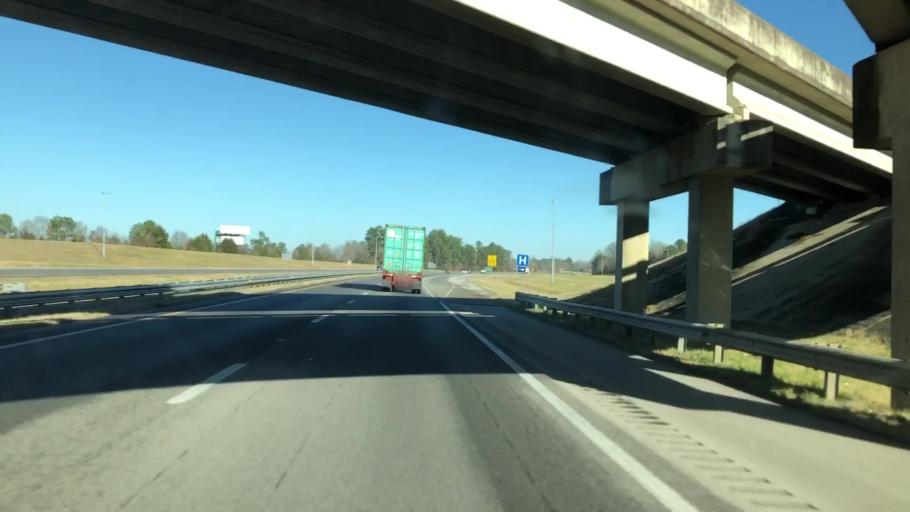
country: US
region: Alabama
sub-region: Limestone County
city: Athens
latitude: 34.8283
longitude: -86.9387
